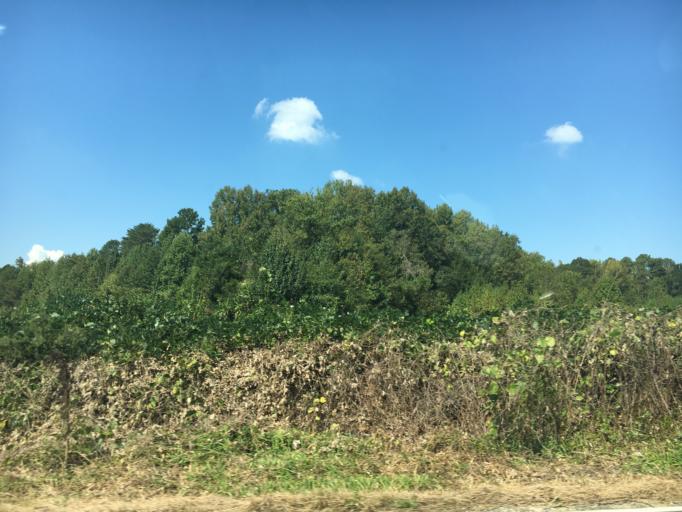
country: US
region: South Carolina
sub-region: Spartanburg County
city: Wellford
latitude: 34.8940
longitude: -82.1007
